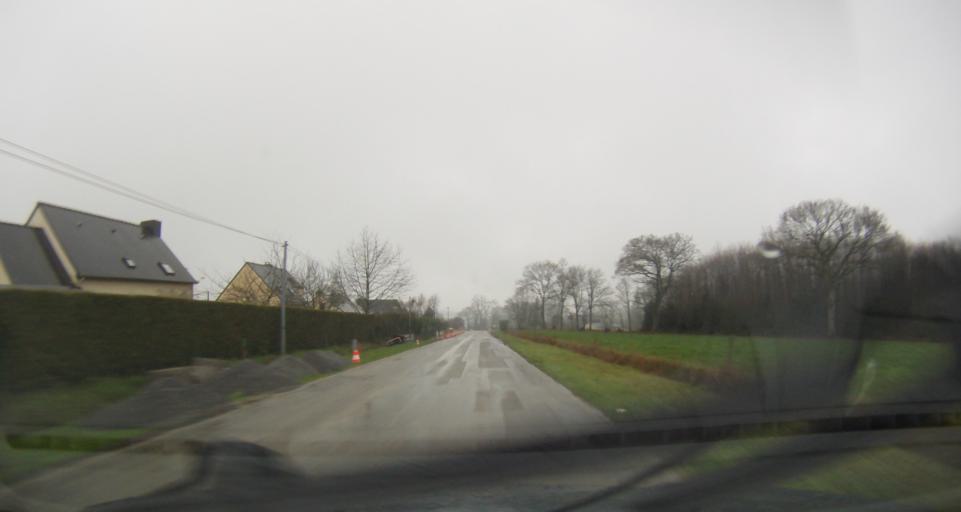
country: FR
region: Brittany
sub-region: Departement d'Ille-et-Vilaine
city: Chanteloup
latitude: 47.9652
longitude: -1.6234
